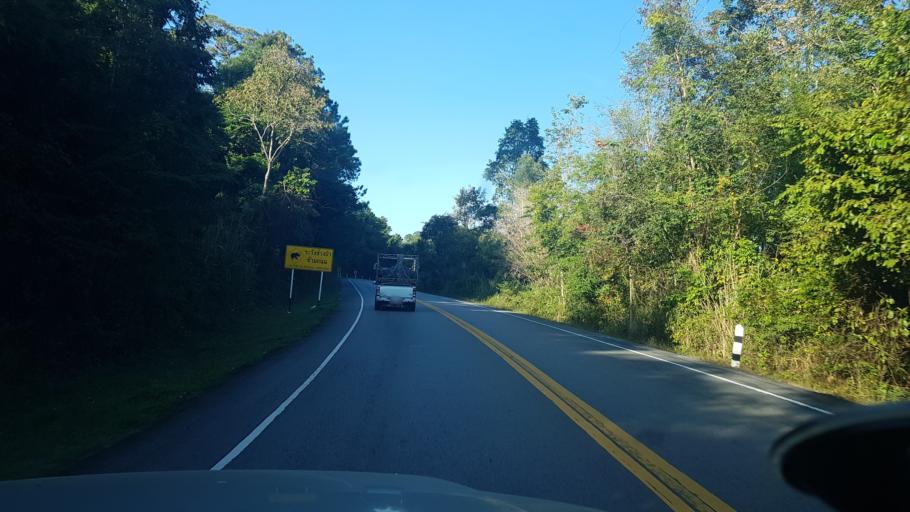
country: TH
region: Phetchabun
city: Nam Nao
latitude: 16.7006
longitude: 101.6219
